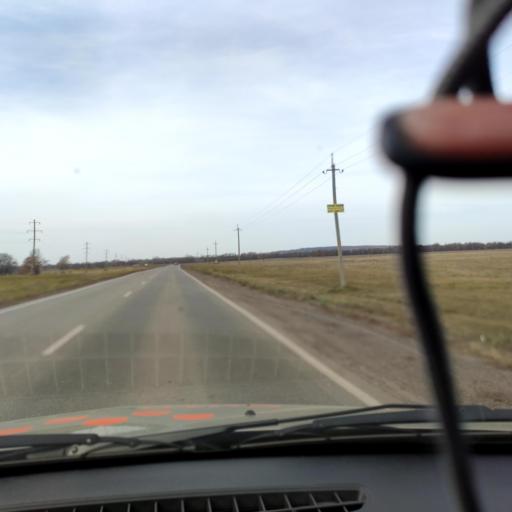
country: RU
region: Bashkortostan
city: Kabakovo
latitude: 54.5563
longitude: 56.0169
